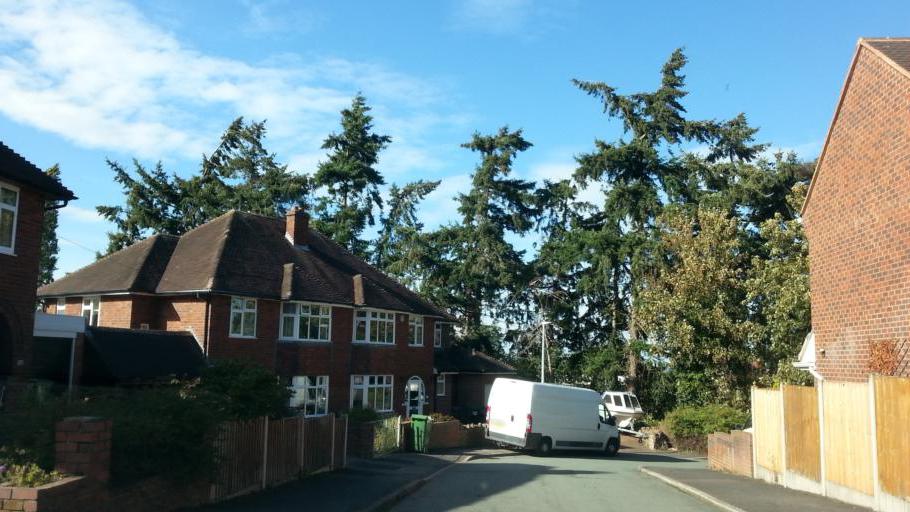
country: GB
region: England
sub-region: Telford and Wrekin
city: Wellington
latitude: 52.6923
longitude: -2.5255
